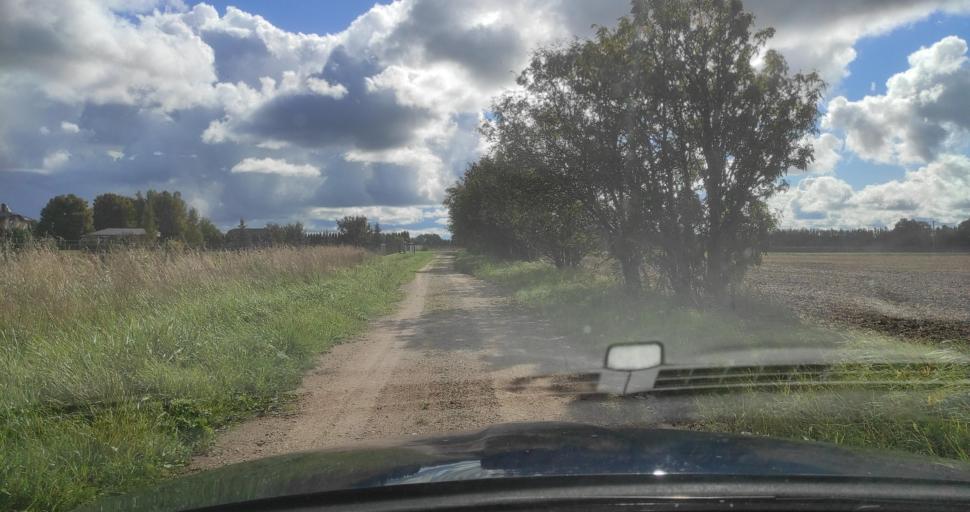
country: LV
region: Ventspils Rajons
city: Piltene
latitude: 57.2681
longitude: 21.6049
